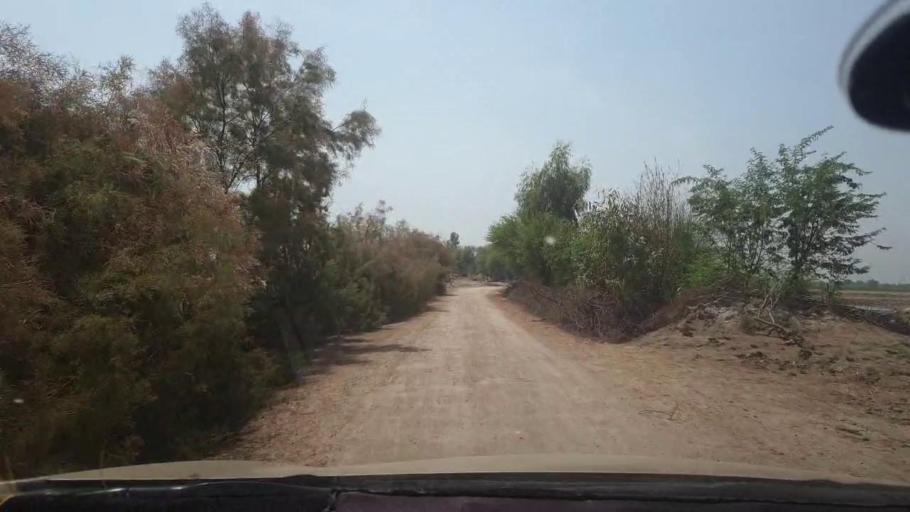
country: PK
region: Sindh
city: Shahdadkot
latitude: 27.7554
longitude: 67.9348
